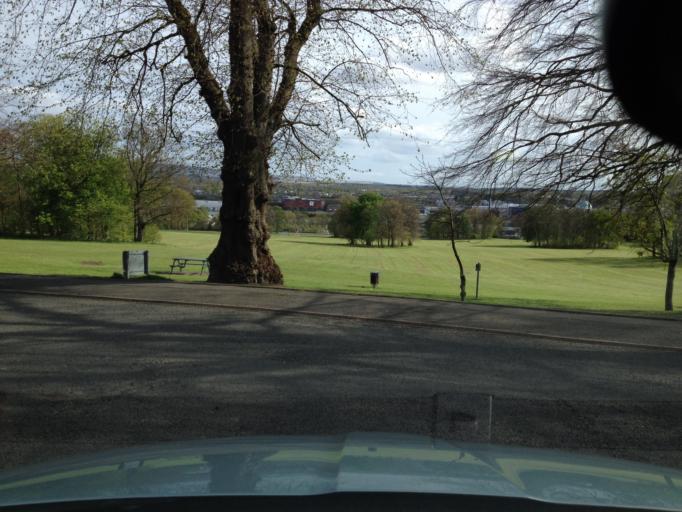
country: GB
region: Scotland
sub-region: West Lothian
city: Livingston
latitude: 55.8927
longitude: -3.5161
